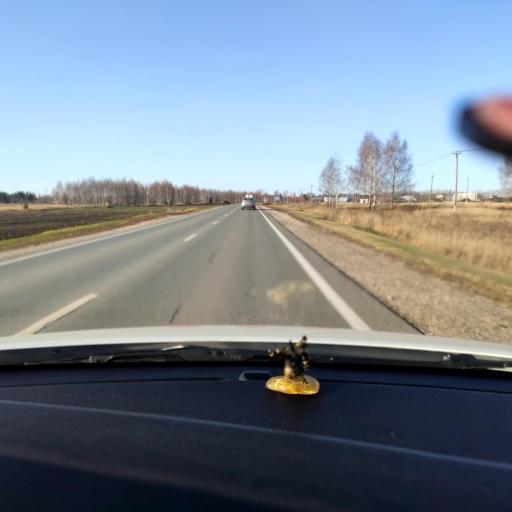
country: RU
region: Tatarstan
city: Stolbishchi
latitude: 55.6164
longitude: 49.1699
